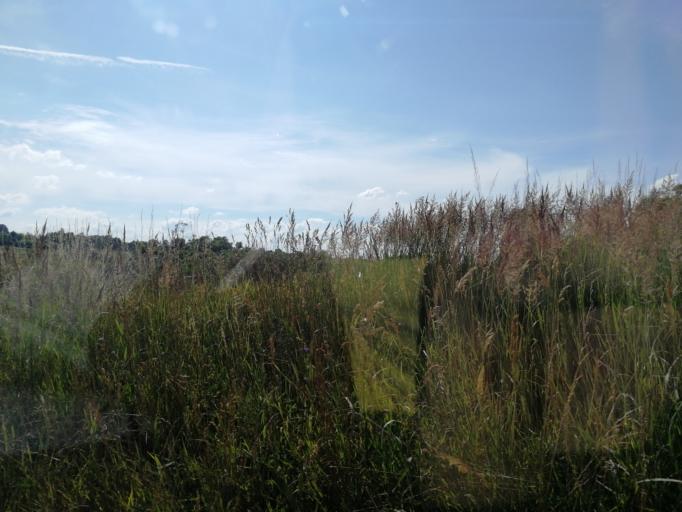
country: RU
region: Tula
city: Tovarkovskiy
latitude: 53.6075
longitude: 38.2722
